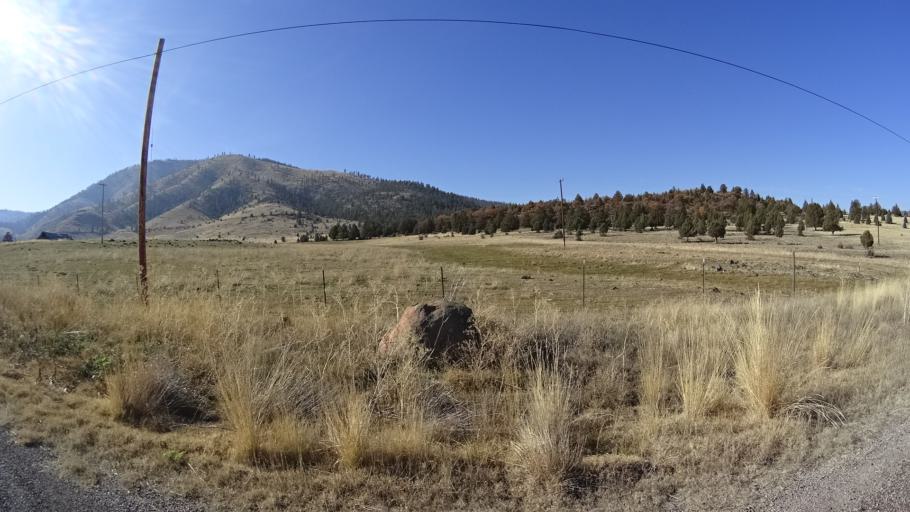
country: US
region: California
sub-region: Siskiyou County
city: Weed
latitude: 41.4926
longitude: -122.5088
